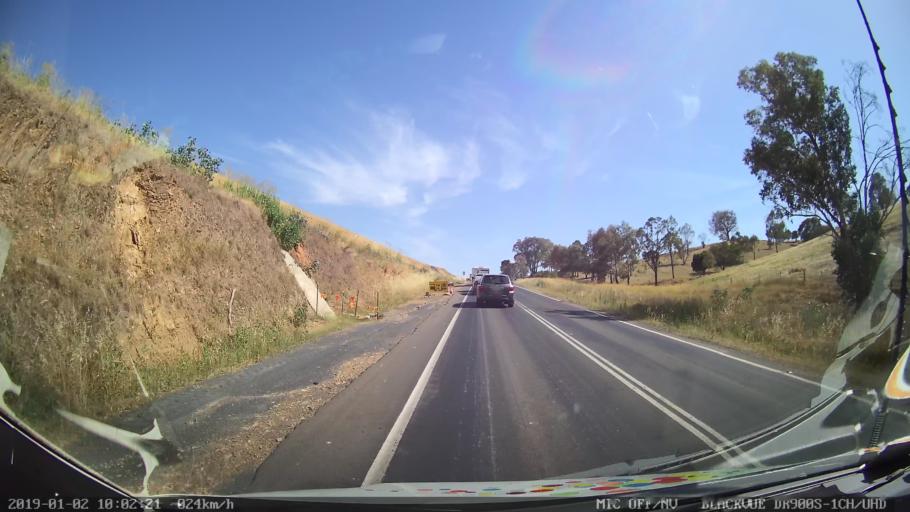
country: AU
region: New South Wales
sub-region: Gundagai
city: Gundagai
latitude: -35.1834
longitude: 148.1264
